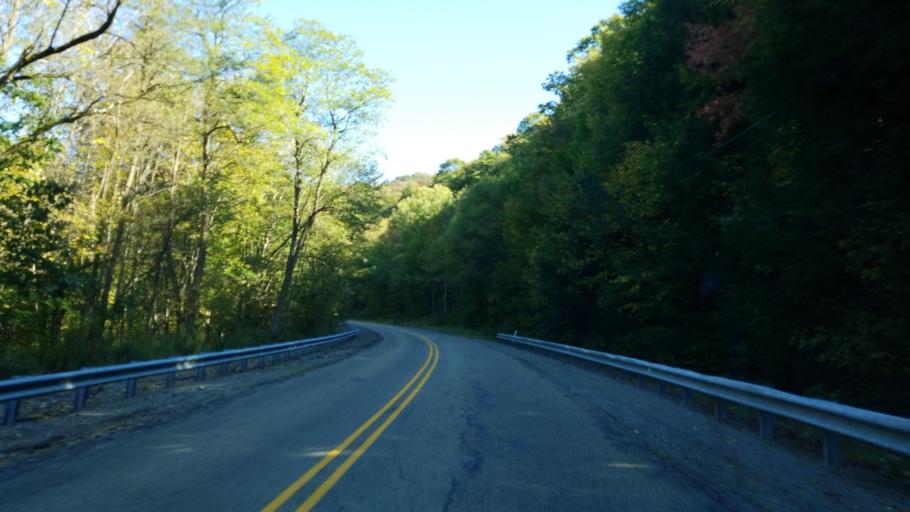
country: US
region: Pennsylvania
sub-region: Clearfield County
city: Shiloh
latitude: 41.2505
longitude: -78.3784
